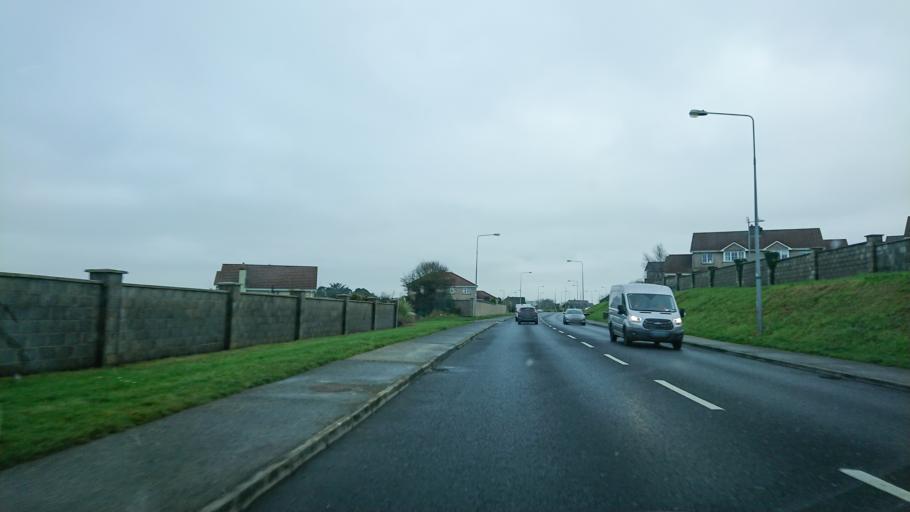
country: IE
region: Munster
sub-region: Waterford
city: Tra Mhor
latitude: 52.1694
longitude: -7.1574
